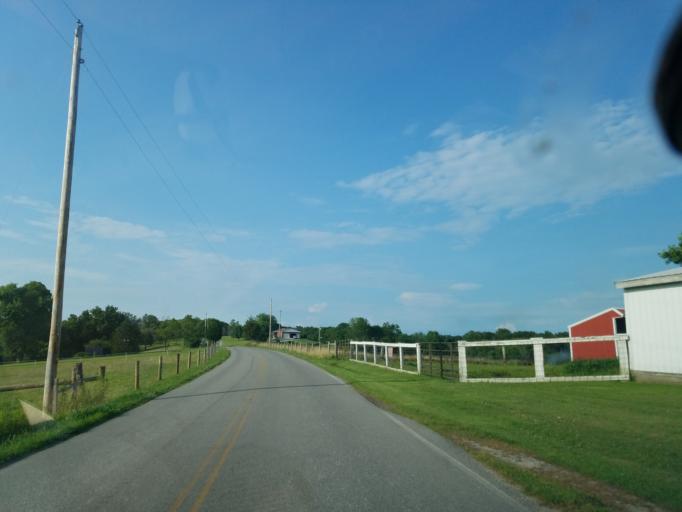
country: US
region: Ohio
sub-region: Adams County
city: West Union
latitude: 38.9039
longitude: -83.5177
